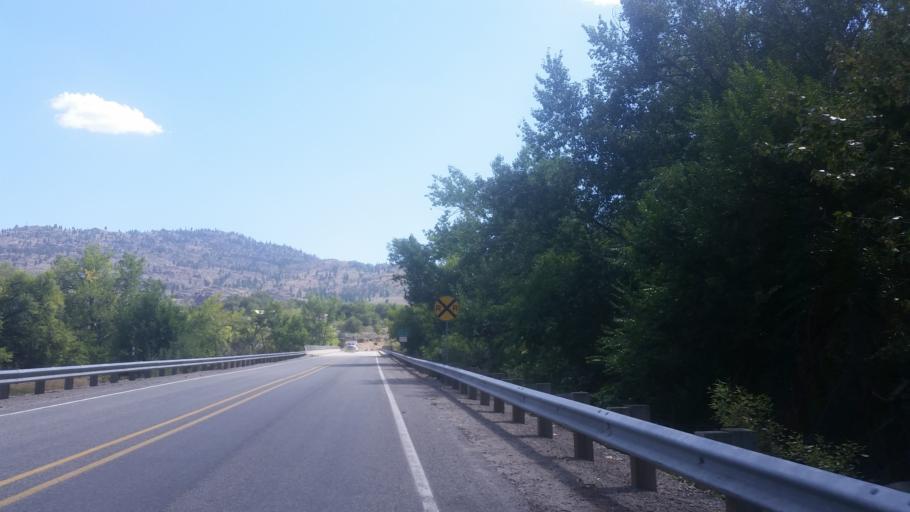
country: US
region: Washington
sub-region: Okanogan County
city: Okanogan
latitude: 48.2818
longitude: -119.7053
